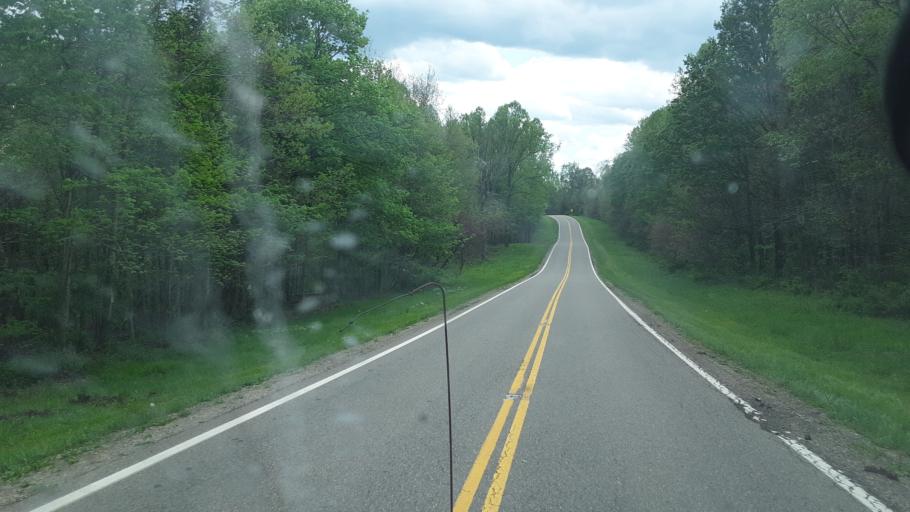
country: US
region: Ohio
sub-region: Noble County
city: Caldwell
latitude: 39.7363
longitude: -81.6478
